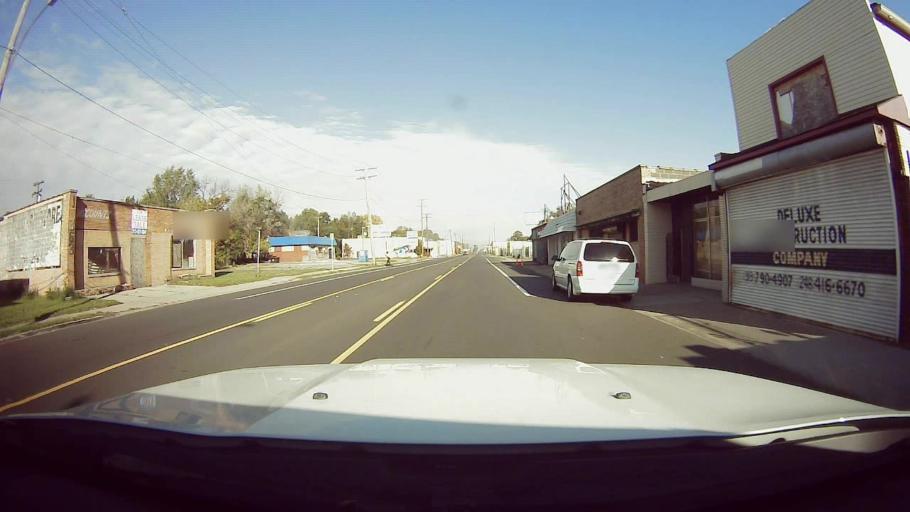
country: US
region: Michigan
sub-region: Oakland County
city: Oak Park
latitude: 42.4032
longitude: -83.1791
